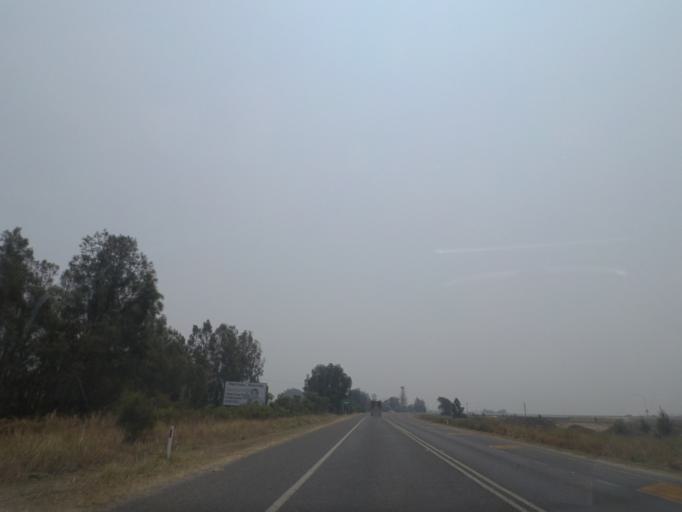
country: AU
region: New South Wales
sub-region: Clarence Valley
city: Maclean
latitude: -29.4214
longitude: 153.2404
